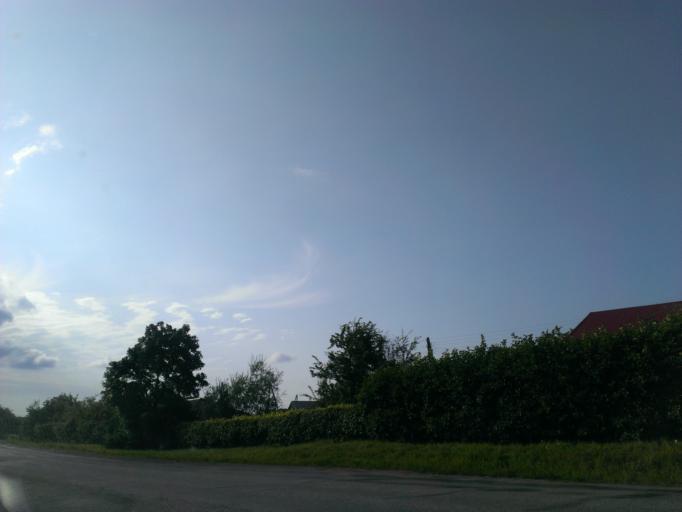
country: LV
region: Priekuli
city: Priekuli
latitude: 57.3095
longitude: 25.3483
